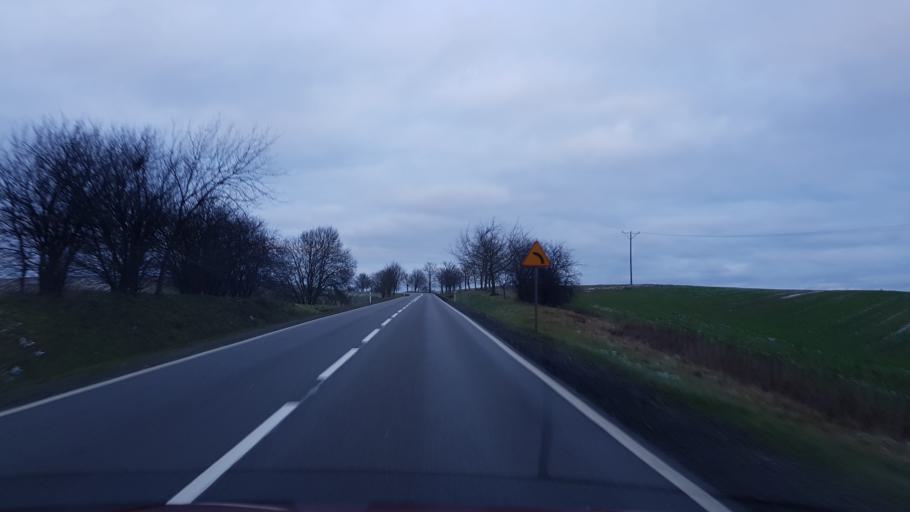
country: PL
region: Pomeranian Voivodeship
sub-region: Powiat czluchowski
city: Koczala
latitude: 54.0283
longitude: 17.1849
